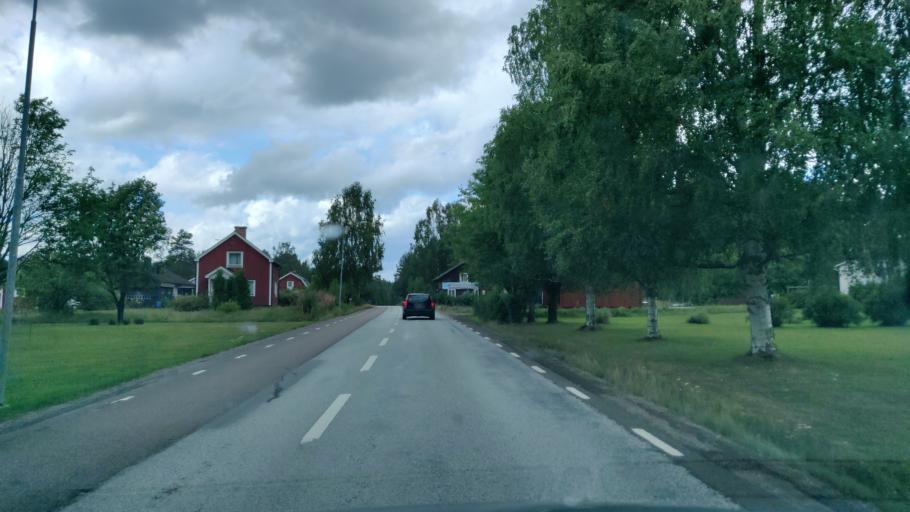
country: SE
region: Vaermland
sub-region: Torsby Kommun
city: Torsby
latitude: 60.6111
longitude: 13.0488
